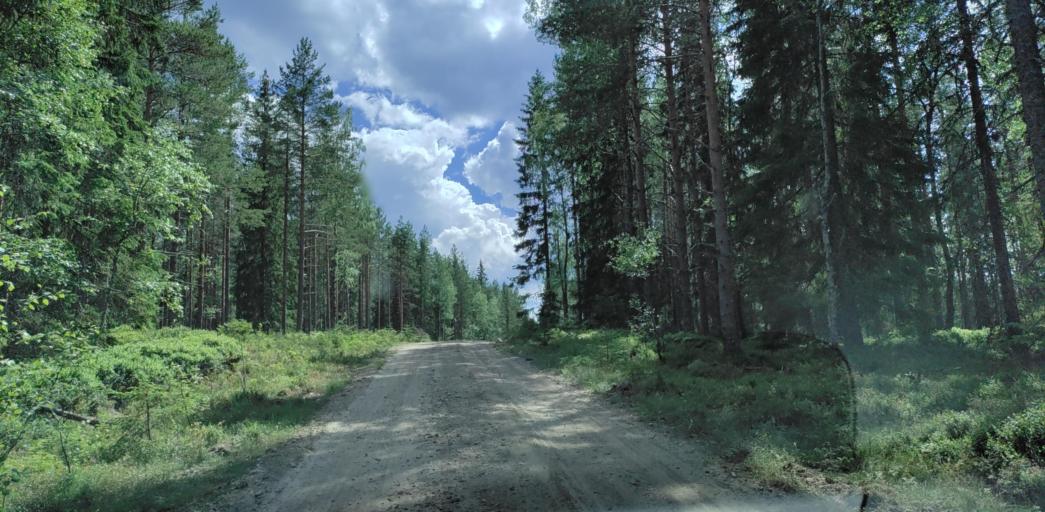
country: SE
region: Vaermland
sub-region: Hagfors Kommun
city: Ekshaerad
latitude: 60.0743
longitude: 13.3454
